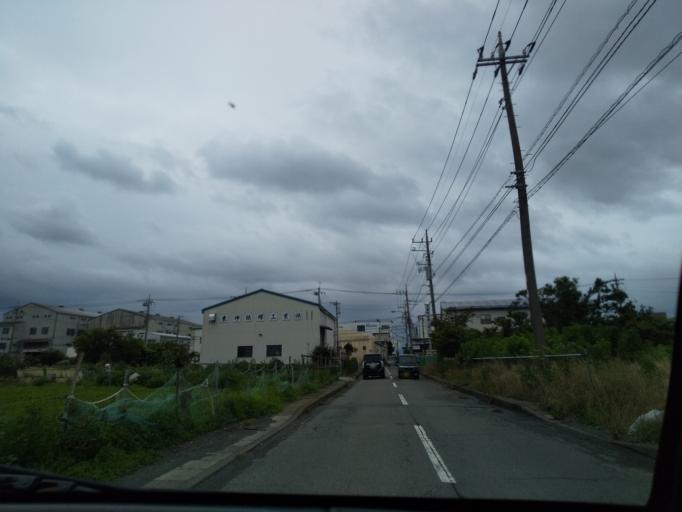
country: JP
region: Kanagawa
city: Minami-rinkan
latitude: 35.4383
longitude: 139.4427
